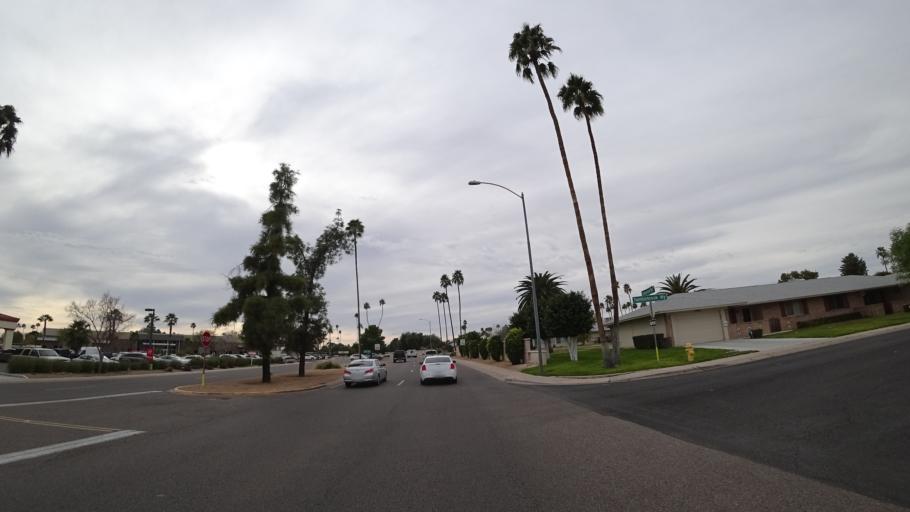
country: US
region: Arizona
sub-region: Maricopa County
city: Sun City
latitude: 33.6094
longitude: -112.2692
